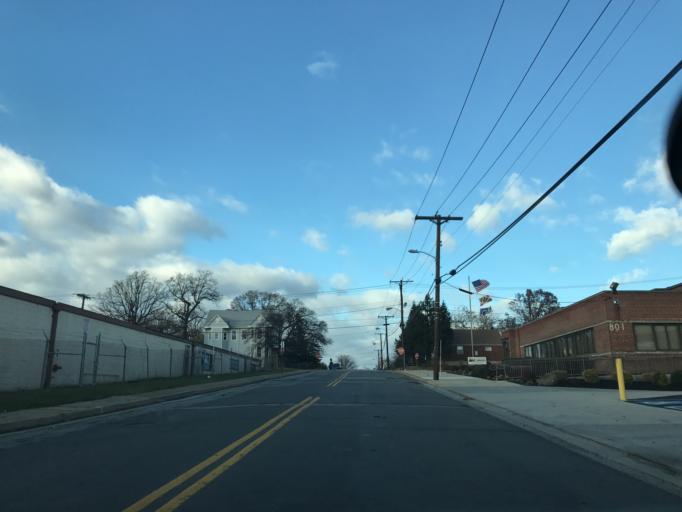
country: US
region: Maryland
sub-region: Baltimore County
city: Rosedale
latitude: 39.3011
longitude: -76.5605
